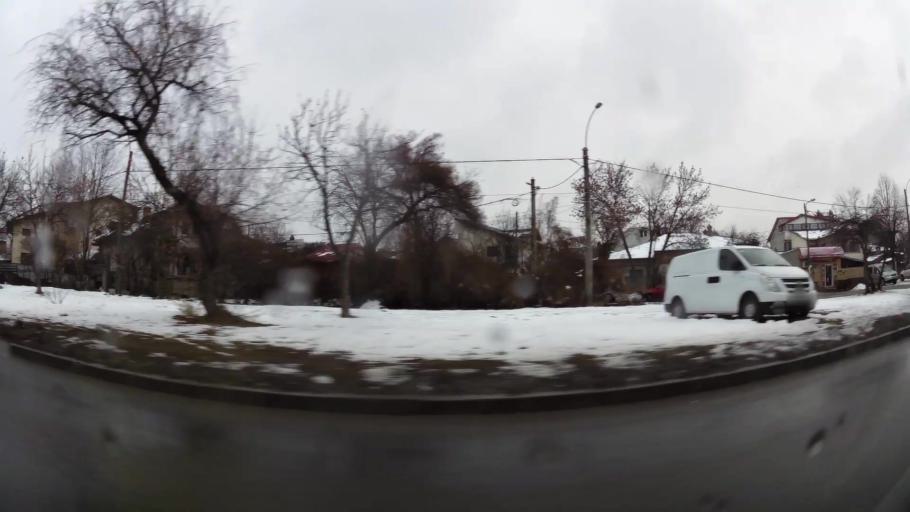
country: RO
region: Ilfov
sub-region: Comuna Chiajna
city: Rosu
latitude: 44.4913
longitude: 26.0276
